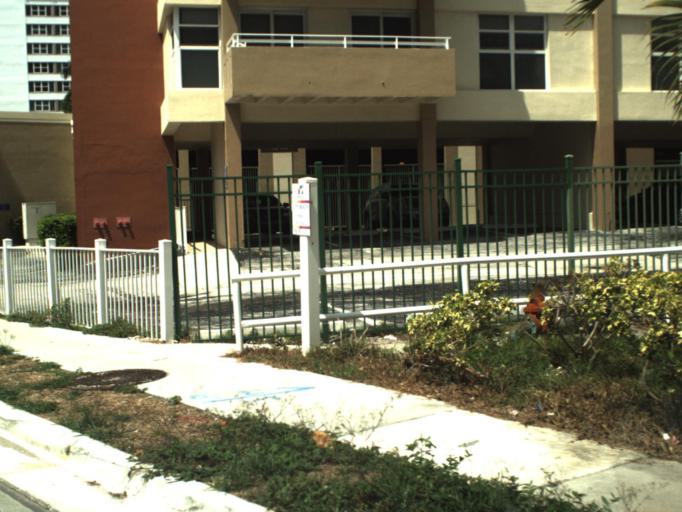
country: US
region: Florida
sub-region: Miami-Dade County
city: Sunny Isles Beach
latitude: 25.9767
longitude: -80.1198
